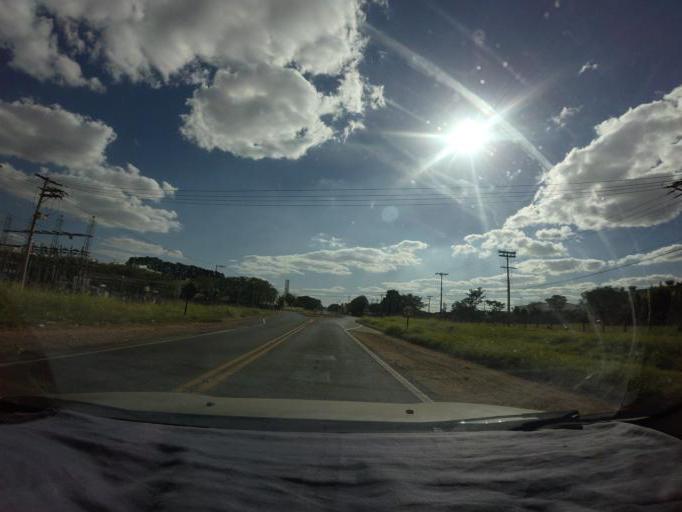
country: BR
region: Sao Paulo
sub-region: Piracicaba
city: Piracicaba
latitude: -22.7392
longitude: -47.5891
